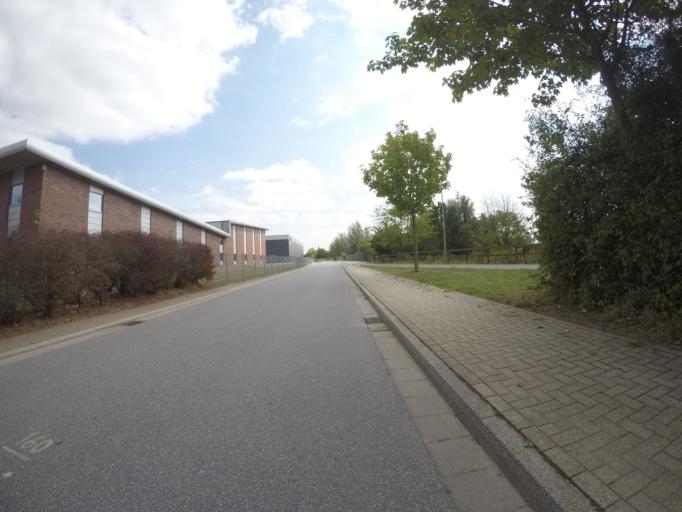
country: DE
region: North Rhine-Westphalia
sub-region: Regierungsbezirk Munster
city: Isselburg
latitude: 51.8178
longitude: 6.4473
